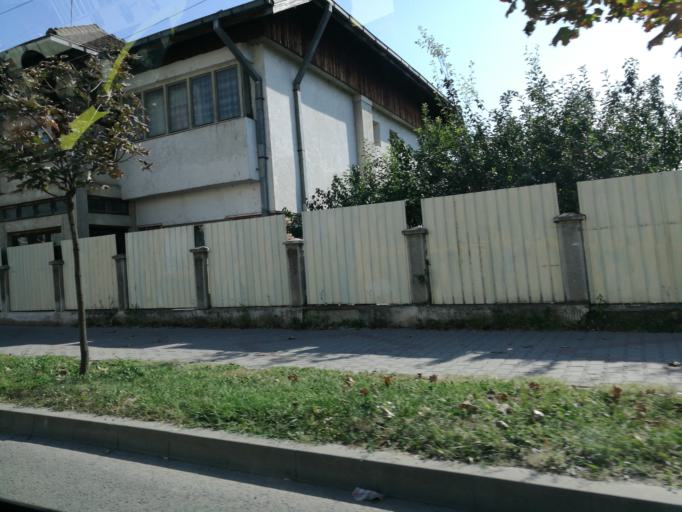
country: RO
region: Iasi
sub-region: Municipiul Iasi
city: Iasi
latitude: 47.1703
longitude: 27.5627
